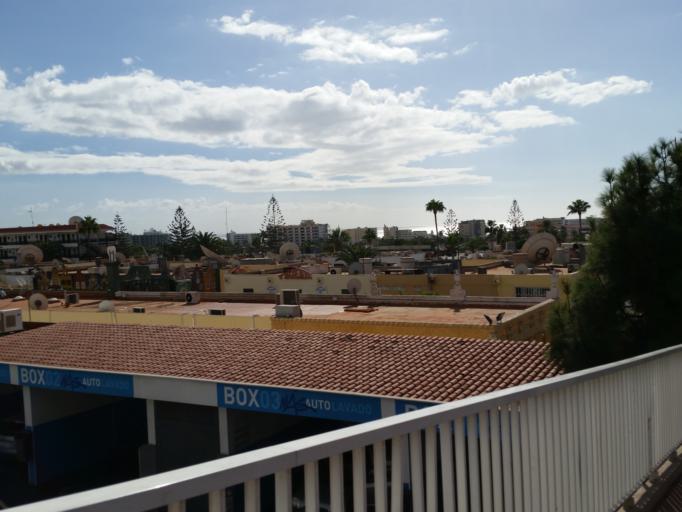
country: ES
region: Canary Islands
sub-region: Provincia de Las Palmas
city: Playa del Ingles
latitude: 27.7638
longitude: -15.5770
